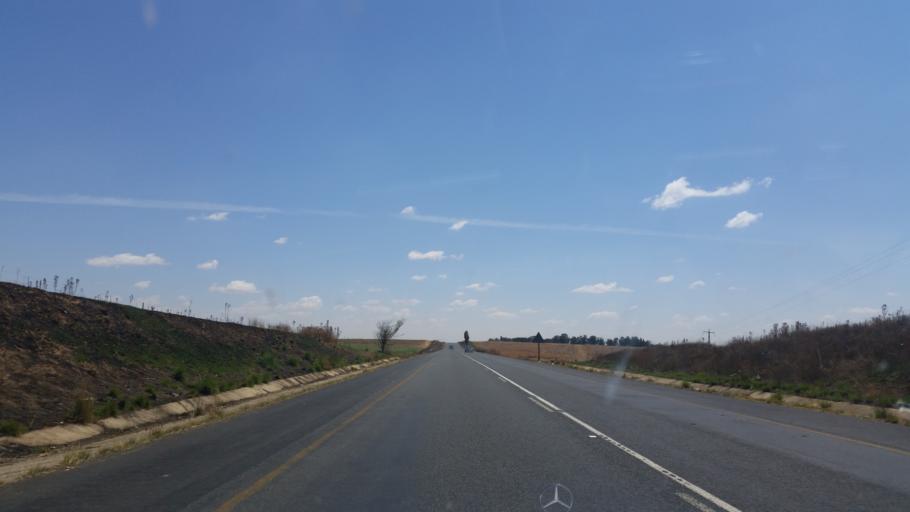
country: ZA
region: Orange Free State
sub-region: Thabo Mofutsanyana District Municipality
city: Bethlehem
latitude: -28.1128
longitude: 28.6738
